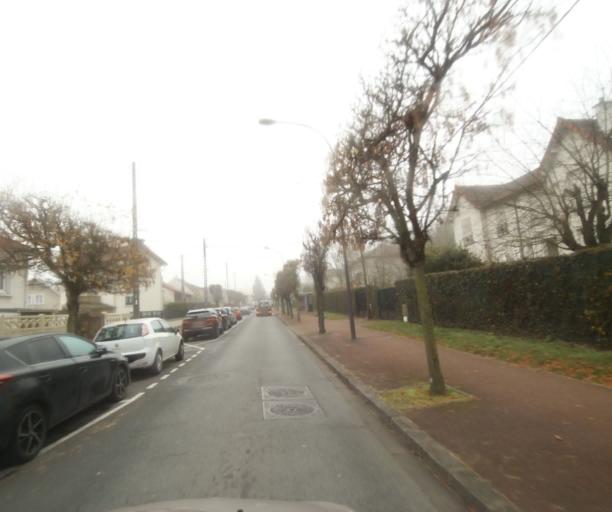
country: FR
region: Ile-de-France
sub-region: Departement de Seine-Saint-Denis
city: Vaujours
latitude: 48.9380
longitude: 2.5687
